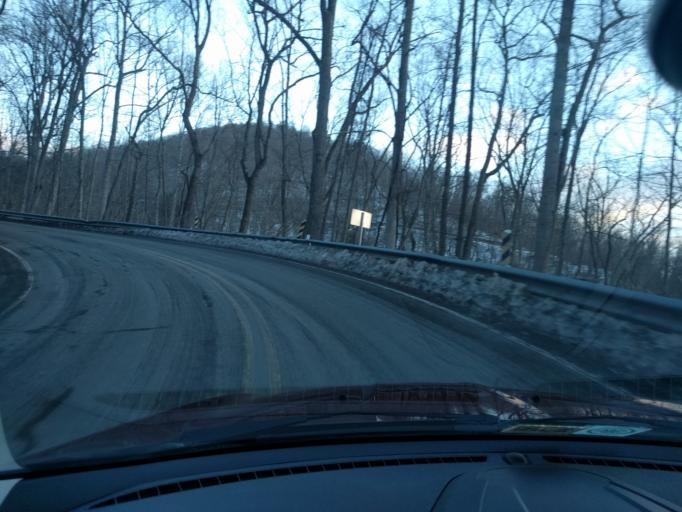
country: US
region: Virginia
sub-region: Bath County
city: Warm Springs
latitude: 38.0924
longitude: -79.8392
